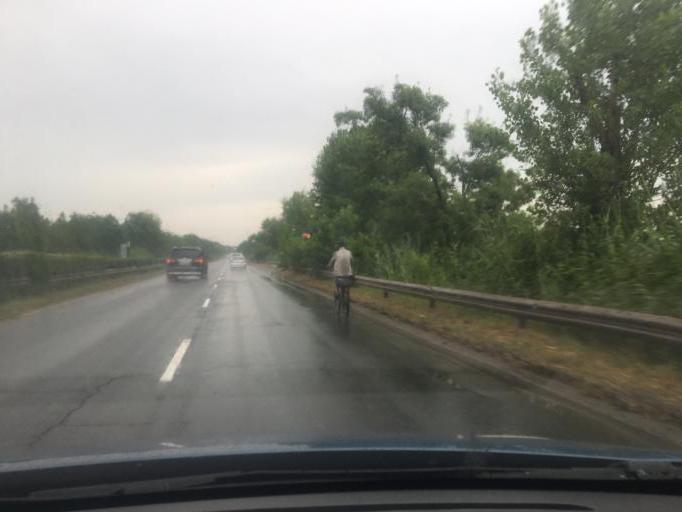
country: BG
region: Burgas
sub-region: Obshtina Burgas
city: Burgas
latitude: 42.5377
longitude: 27.4718
